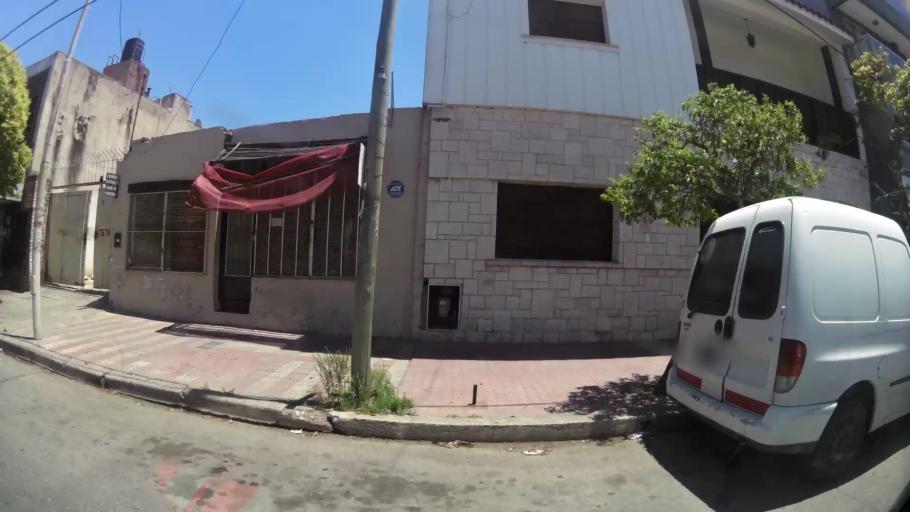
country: AR
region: Cordoba
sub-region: Departamento de Capital
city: Cordoba
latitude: -31.4035
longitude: -64.2185
